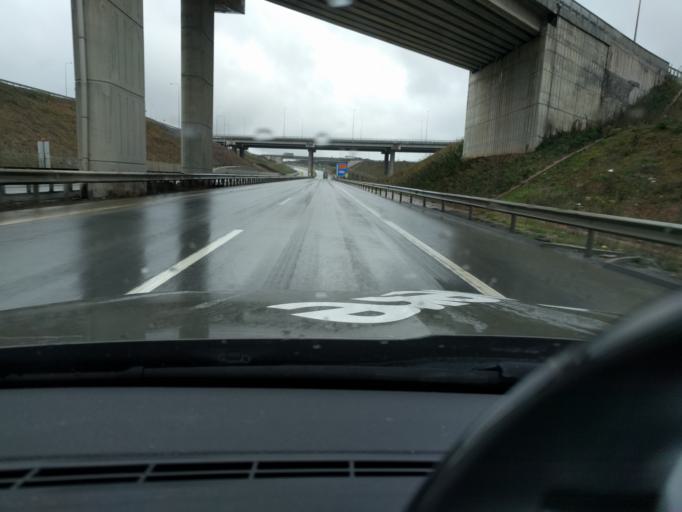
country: TR
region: Istanbul
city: Kemerburgaz
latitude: 41.2298
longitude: 28.8460
